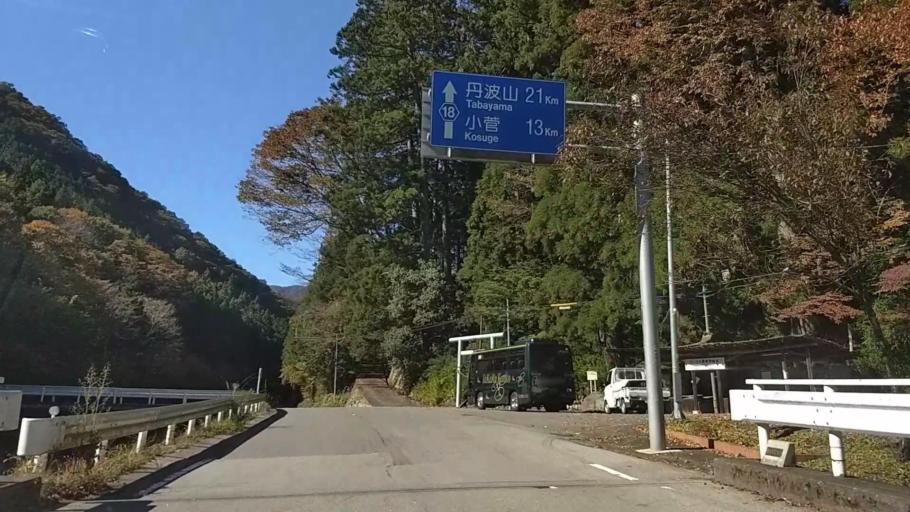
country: JP
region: Yamanashi
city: Otsuki
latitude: 35.7054
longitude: 139.0128
